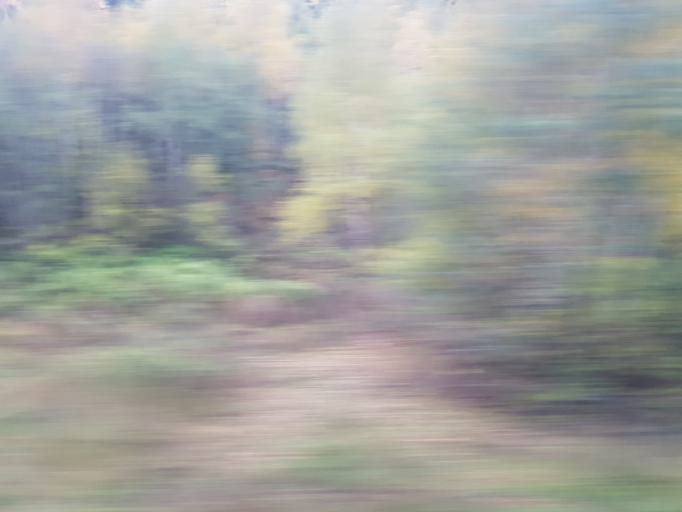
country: NO
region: Oppland
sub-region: Sel
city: Otta
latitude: 61.8397
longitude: 9.4424
